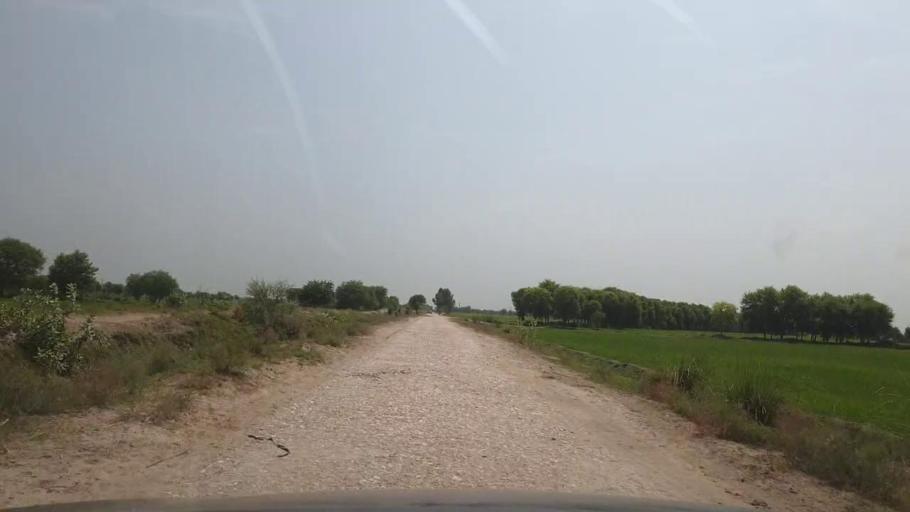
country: PK
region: Sindh
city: Ratodero
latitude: 27.8804
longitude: 68.3446
